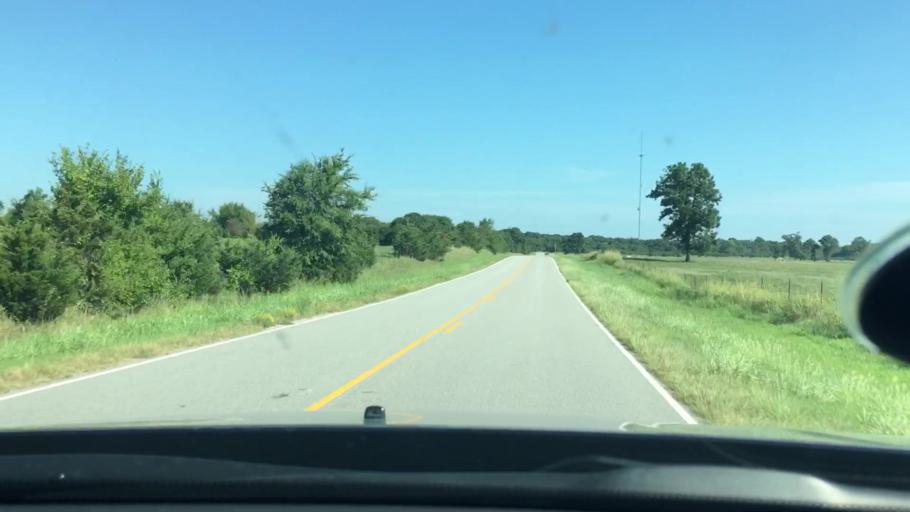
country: US
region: Oklahoma
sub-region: Johnston County
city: Tishomingo
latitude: 34.3539
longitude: -96.5488
